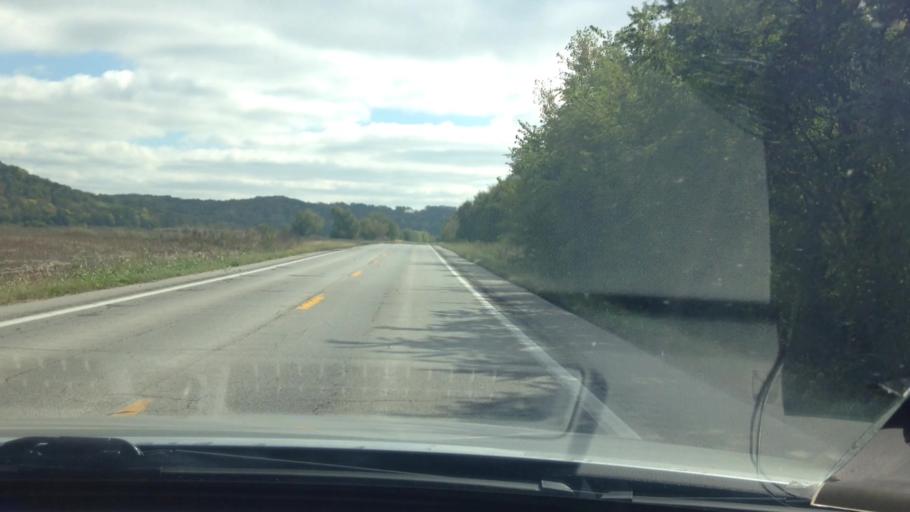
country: US
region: Kansas
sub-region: Leavenworth County
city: Lansing
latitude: 39.2638
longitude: -94.8156
